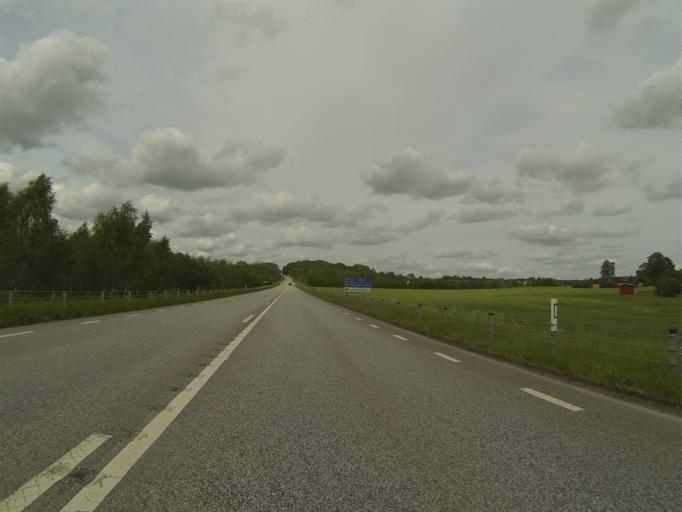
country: SE
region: Skane
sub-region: Sjobo Kommun
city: Sjoebo
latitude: 55.6512
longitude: 13.6972
